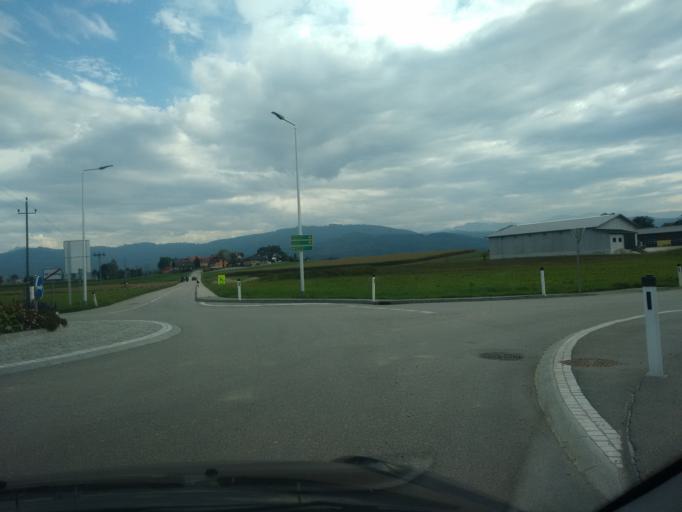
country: AT
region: Upper Austria
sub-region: Politischer Bezirk Vocklabruck
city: Lenzing
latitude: 47.9678
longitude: 13.6278
